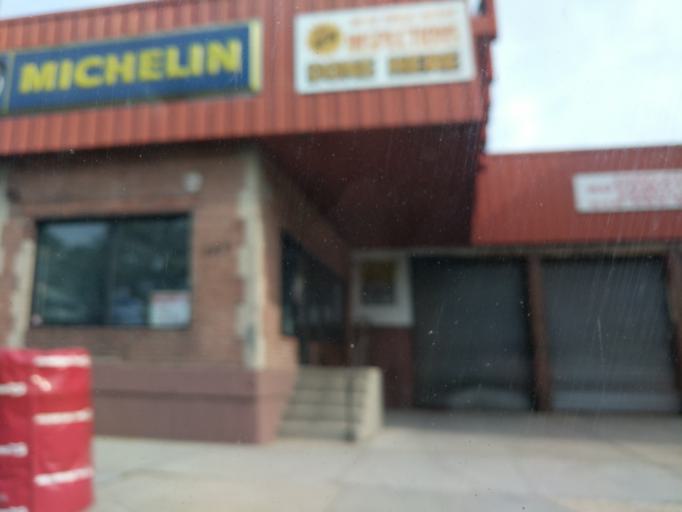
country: US
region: New York
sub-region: Nassau County
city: Lynbrook
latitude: 40.6555
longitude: -73.6673
